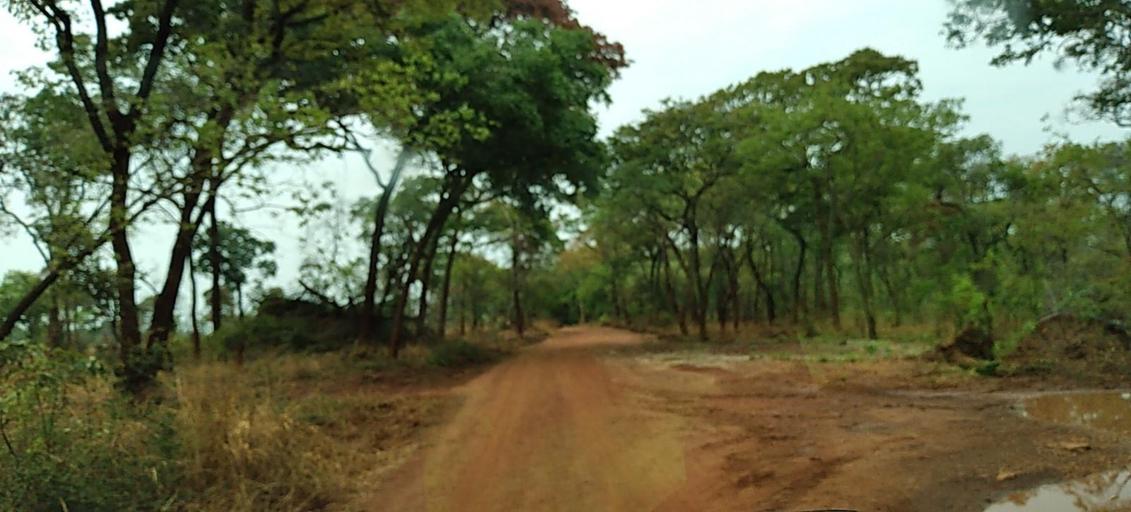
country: ZM
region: North-Western
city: Solwezi
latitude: -12.3130
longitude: 26.5223
